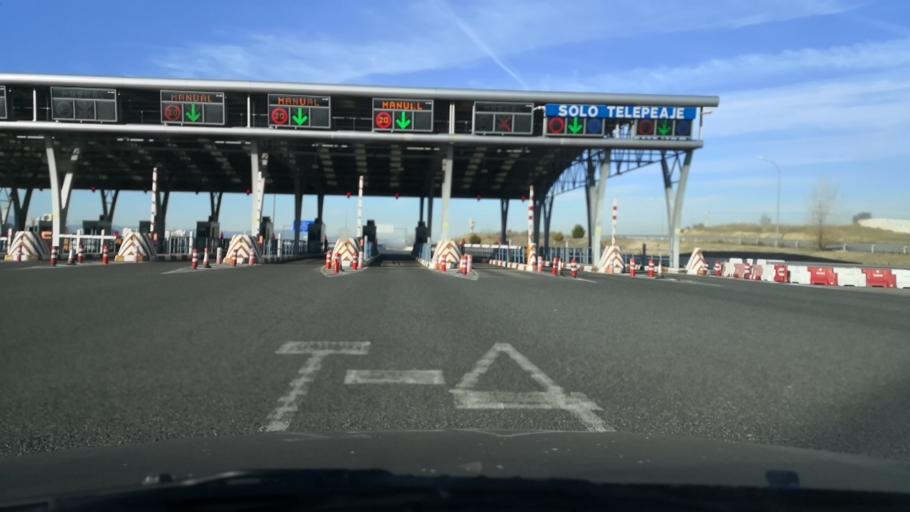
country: ES
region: Madrid
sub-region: Provincia de Madrid
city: Barajas de Madrid
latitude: 40.4768
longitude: -3.6012
